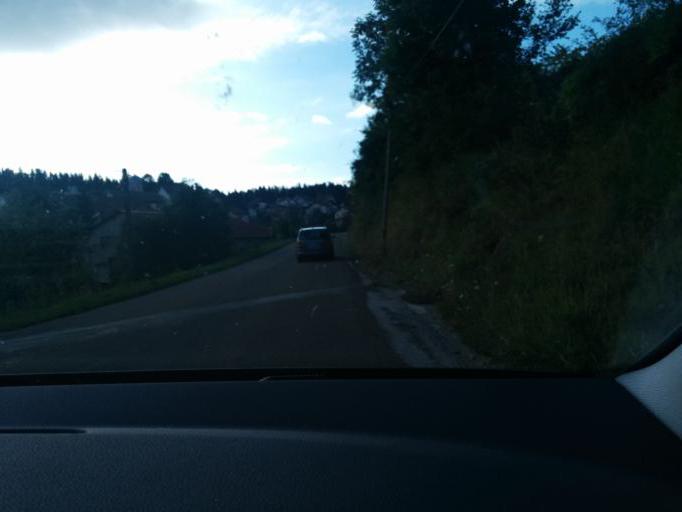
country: FR
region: Franche-Comte
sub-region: Departement du Jura
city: Saint-Lupicin
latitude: 46.4591
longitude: 5.7970
